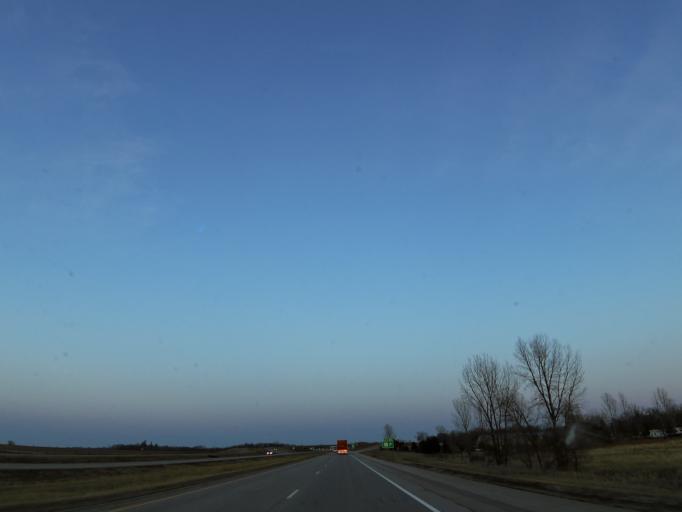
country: US
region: Minnesota
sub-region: Mower County
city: Austin
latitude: 43.6735
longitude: -92.8018
